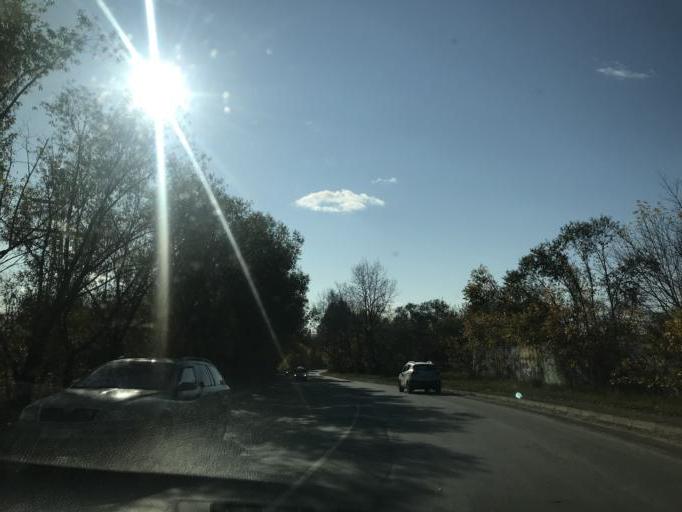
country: RU
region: Chelyabinsk
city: Dolgoderevenskoye
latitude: 55.2562
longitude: 61.3587
